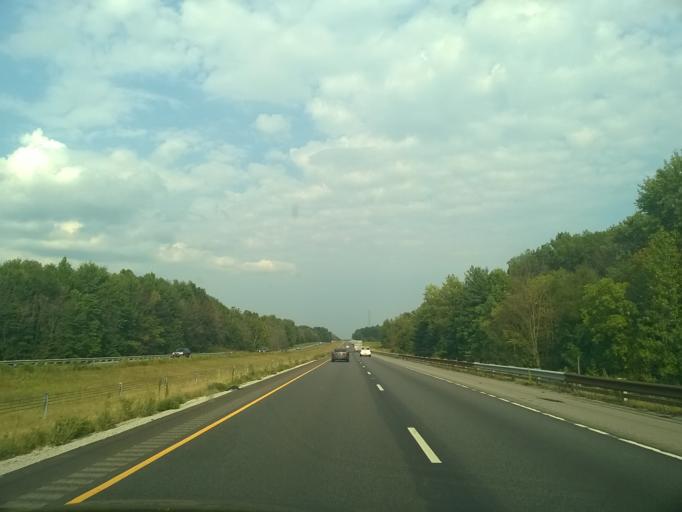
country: US
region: Indiana
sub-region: Clay County
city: Brazil
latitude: 39.4643
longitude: -87.0649
